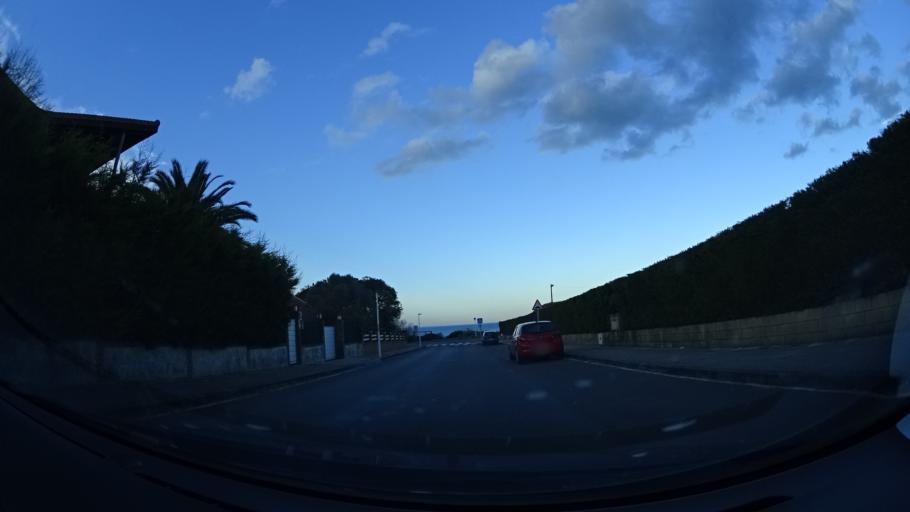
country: ES
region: Basque Country
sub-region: Bizkaia
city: Plentzia
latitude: 43.4074
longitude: -2.9621
